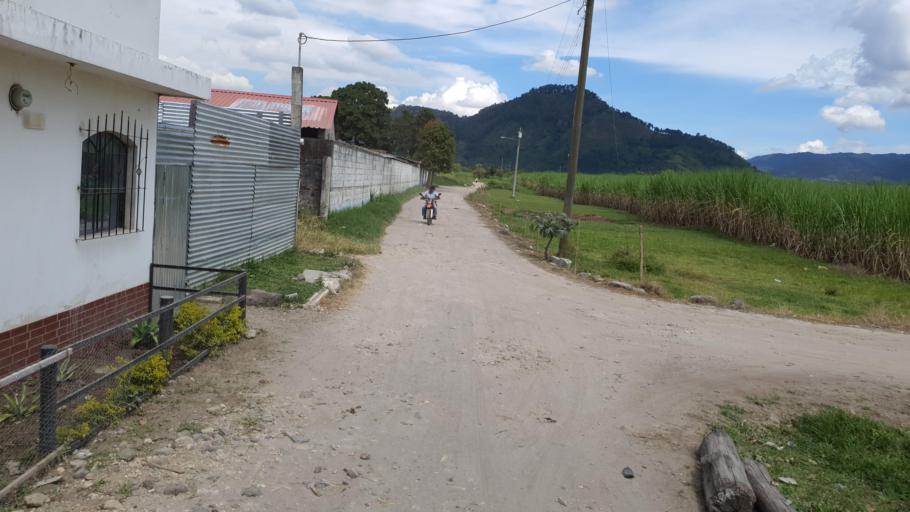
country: GT
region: Guatemala
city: Villa Canales
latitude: 14.4563
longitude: -90.5562
